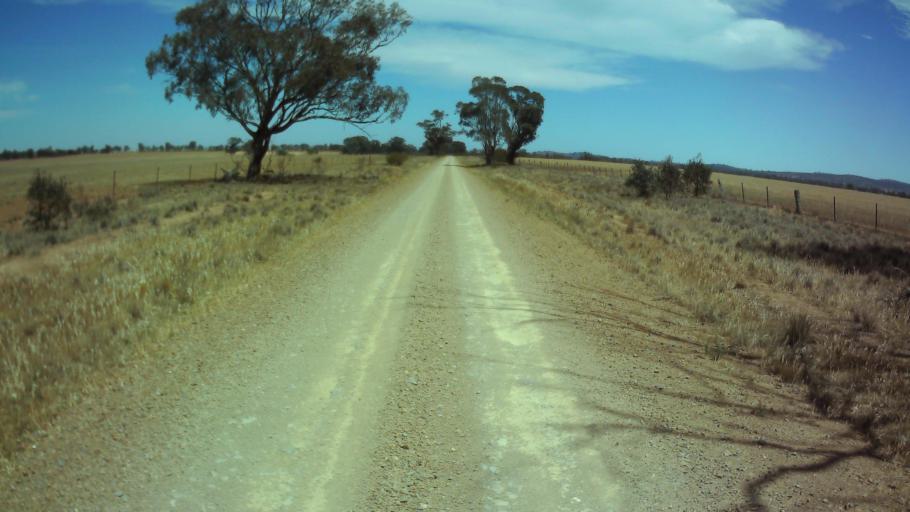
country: AU
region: New South Wales
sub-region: Weddin
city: Grenfell
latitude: -33.8584
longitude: 147.9220
